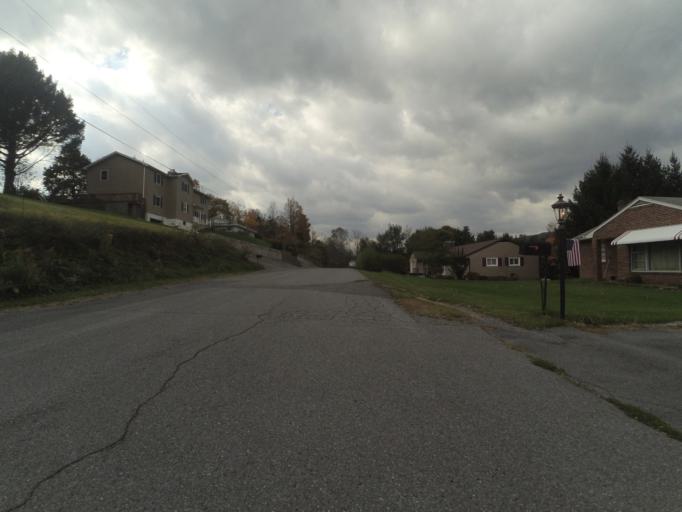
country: US
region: Pennsylvania
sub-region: Centre County
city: Bellefonte
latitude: 40.9039
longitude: -77.7906
